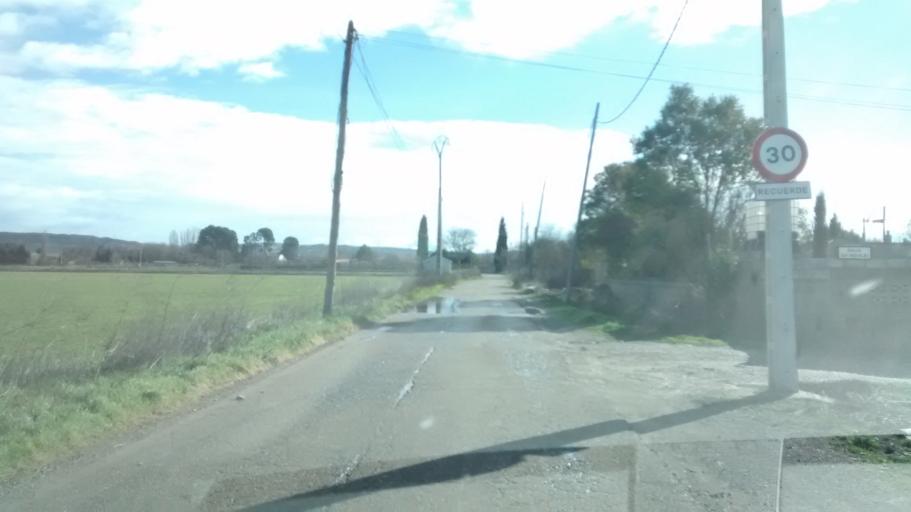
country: ES
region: Aragon
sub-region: Provincia de Zaragoza
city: Villanueva de Gallego
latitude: 41.7302
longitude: -0.7913
